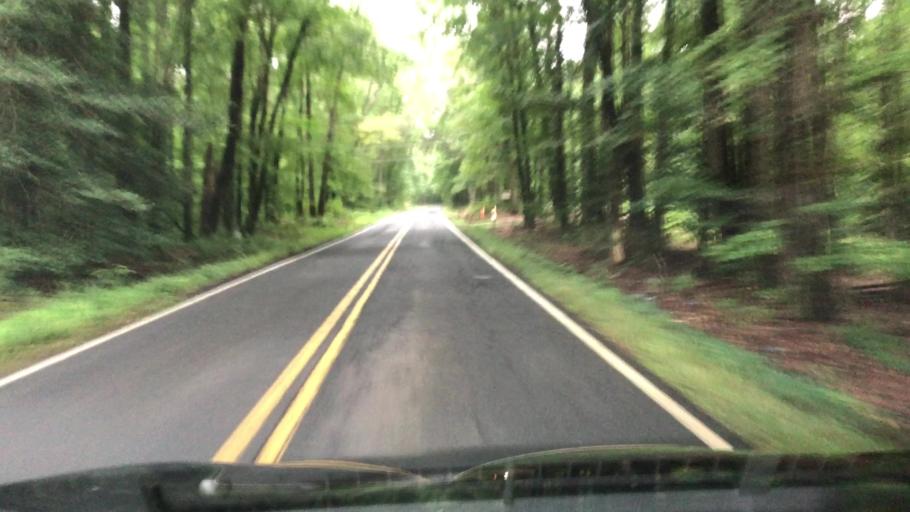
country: US
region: Virginia
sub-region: Fauquier County
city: Bealeton
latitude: 38.5039
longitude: -77.6010
